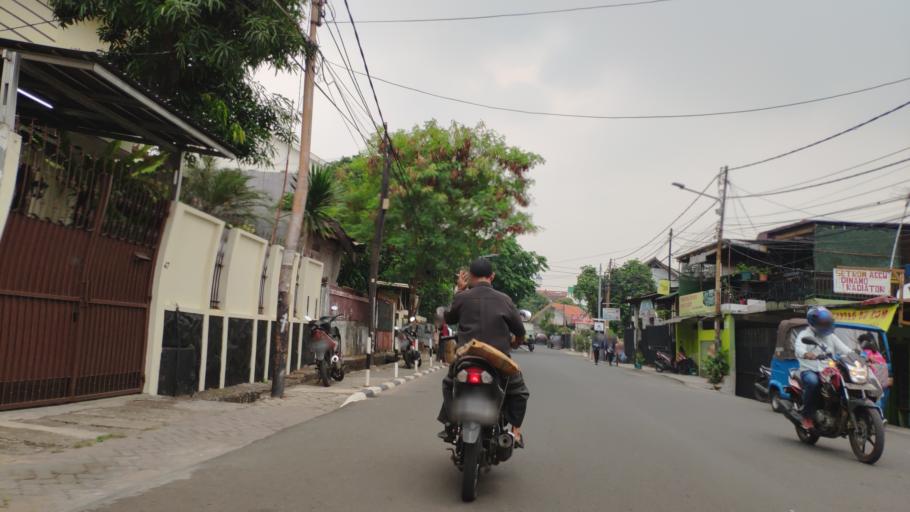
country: ID
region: Jakarta Raya
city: Jakarta
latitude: -6.2530
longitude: 106.7946
